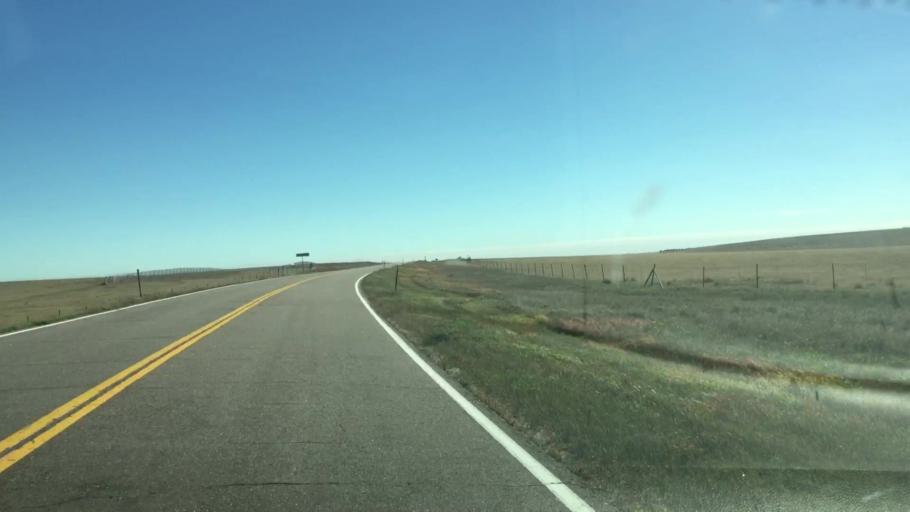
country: US
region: Colorado
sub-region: Lincoln County
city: Limon
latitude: 39.2879
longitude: -103.9738
